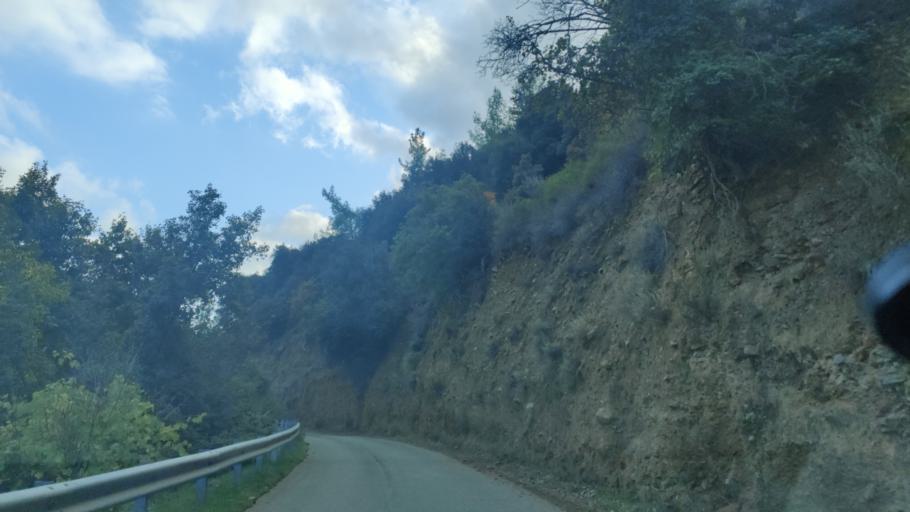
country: CY
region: Lefkosia
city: Lefka
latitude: 35.0561
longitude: 32.7348
